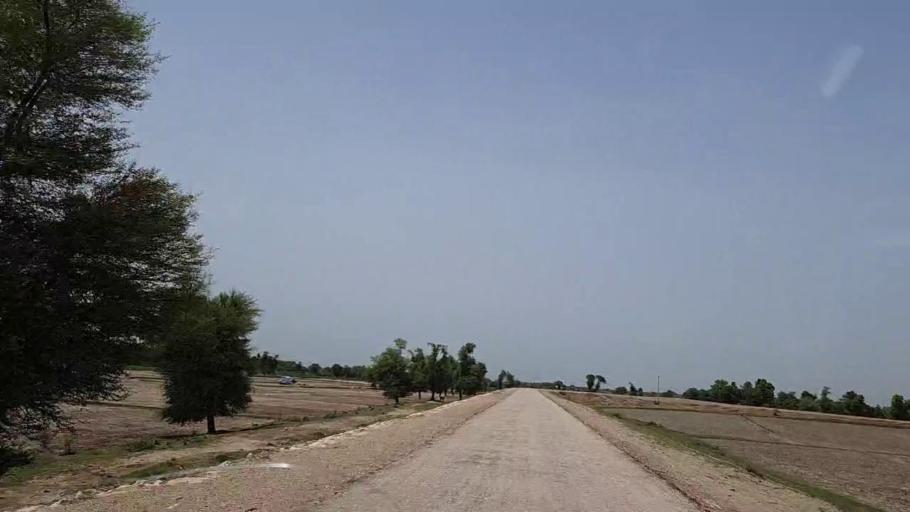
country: PK
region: Sindh
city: Tharu Shah
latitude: 27.0089
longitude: 68.1026
